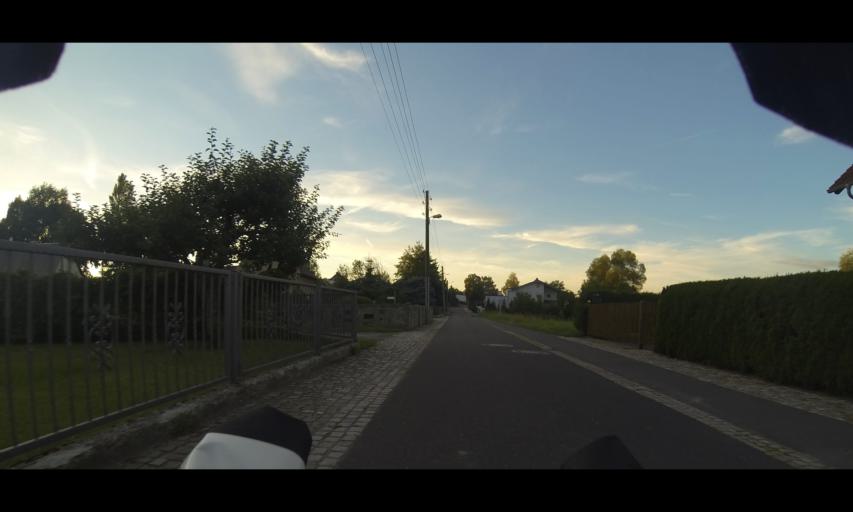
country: DE
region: Saxony
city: Radeburg
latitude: 51.2032
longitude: 13.7272
